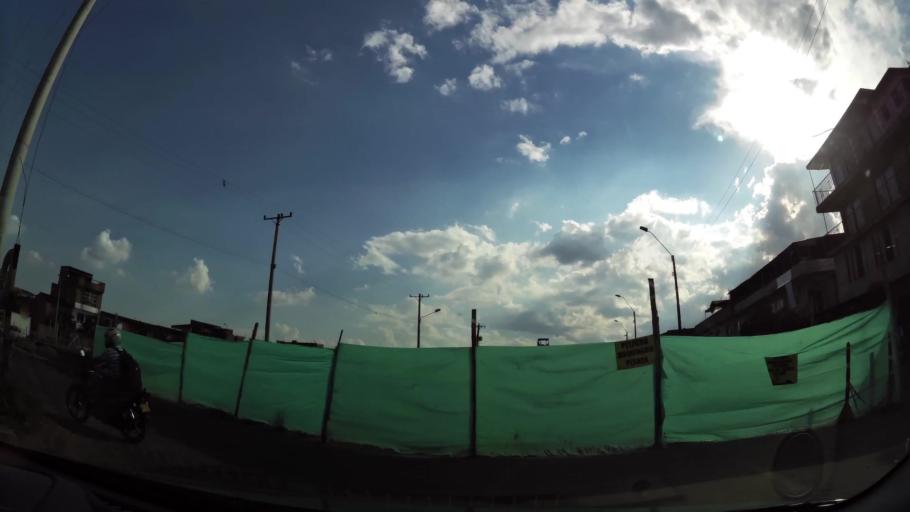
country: CO
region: Valle del Cauca
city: Cali
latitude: 3.3949
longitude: -76.5120
